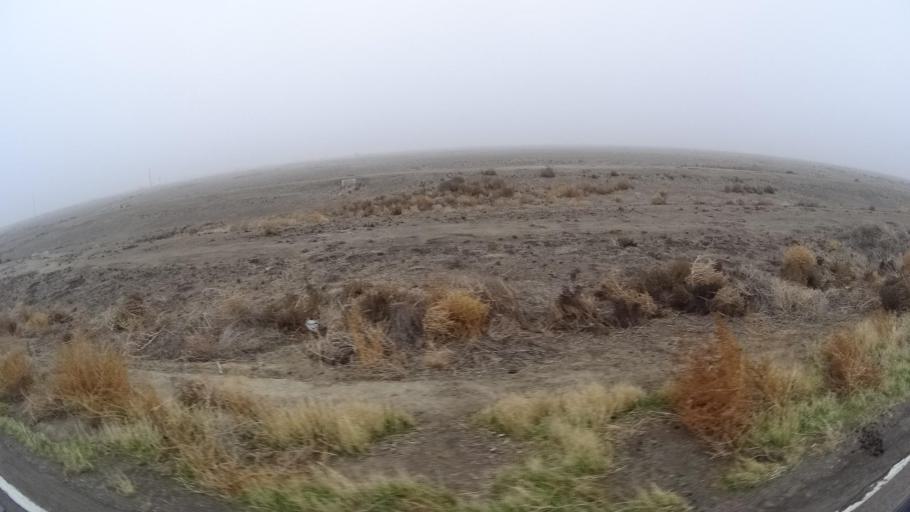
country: US
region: California
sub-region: Kern County
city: Lost Hills
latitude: 35.6084
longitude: -119.6174
